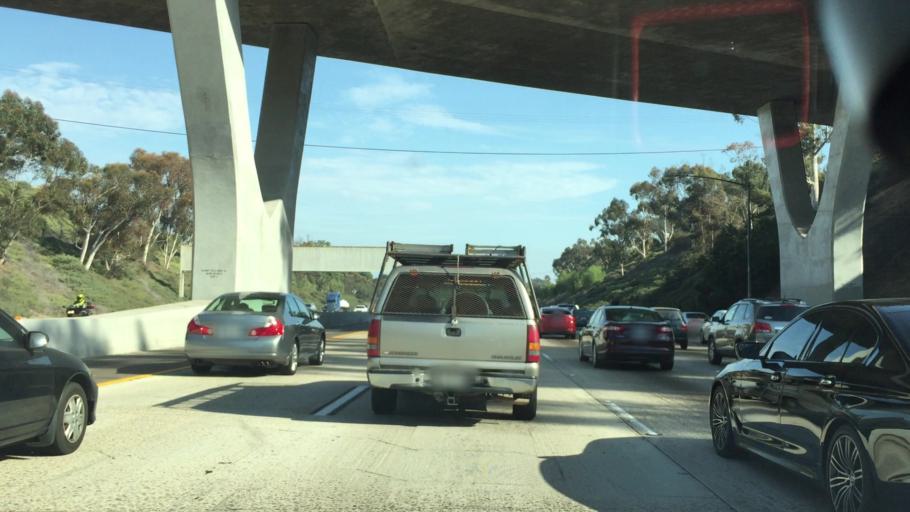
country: US
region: California
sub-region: San Diego County
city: San Diego
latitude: 32.8041
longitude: -117.1510
